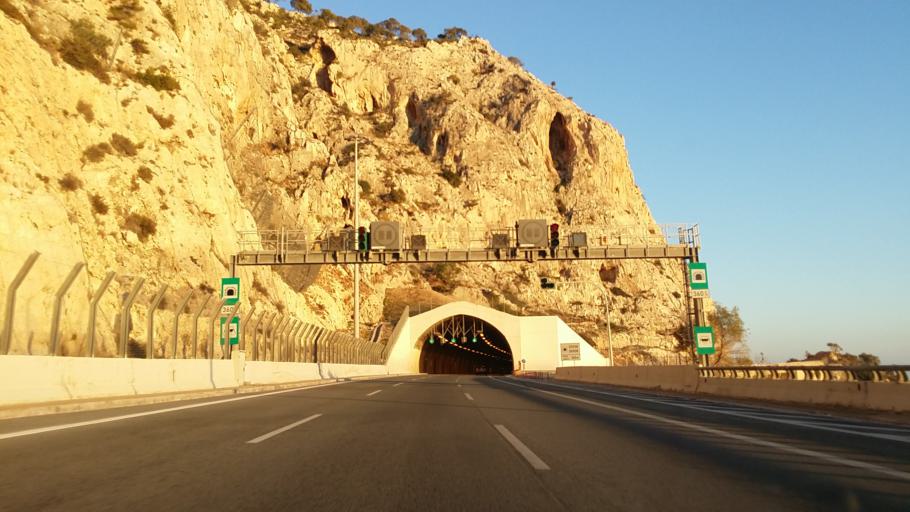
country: GR
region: Attica
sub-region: Nomarchia Dytikis Attikis
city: Megara
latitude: 37.9785
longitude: 23.2793
